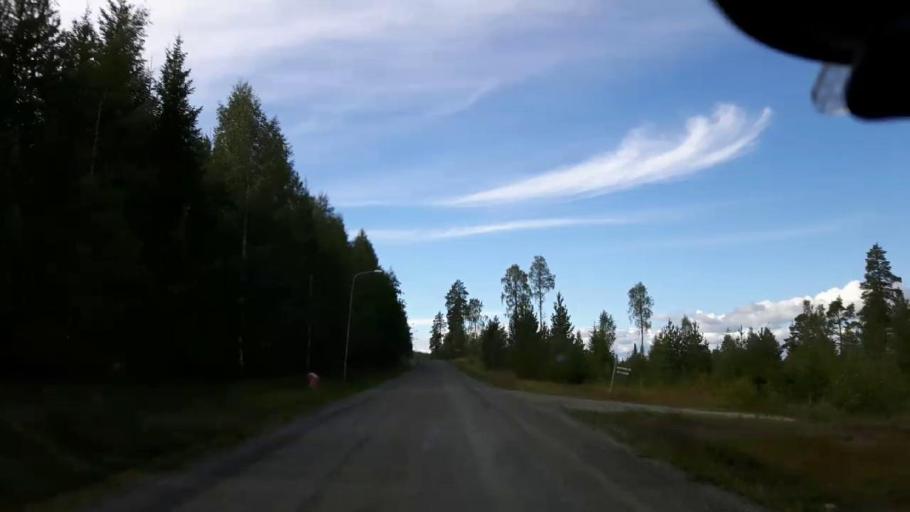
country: SE
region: Jaemtland
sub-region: Ragunda Kommun
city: Hammarstrand
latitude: 63.1397
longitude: 15.9286
